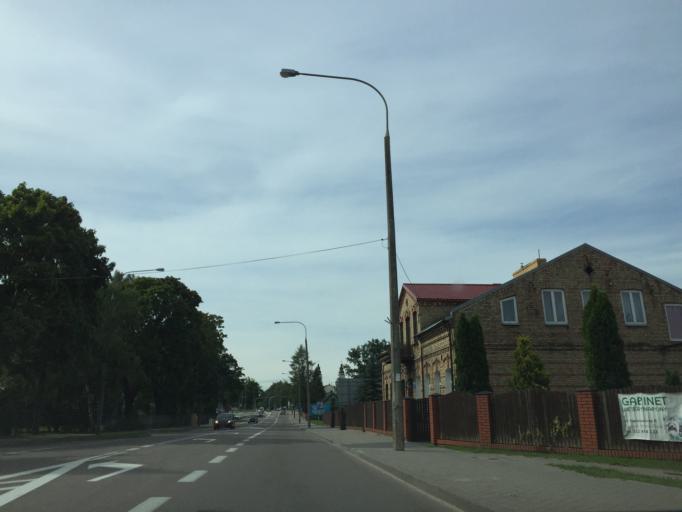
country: PL
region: Podlasie
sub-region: Suwalki
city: Suwalki
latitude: 54.0913
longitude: 22.9291
